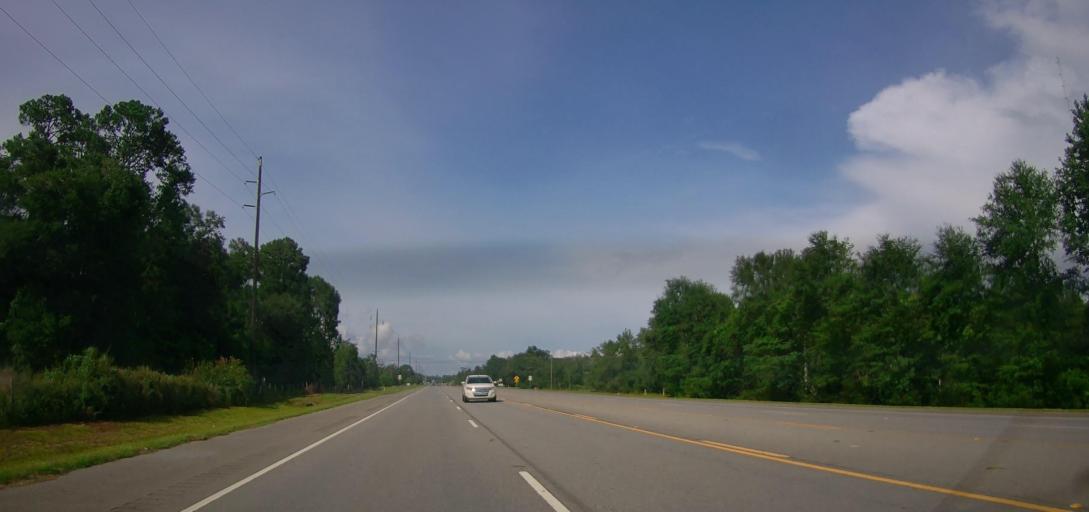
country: US
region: Georgia
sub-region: Wayne County
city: Jesup
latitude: 31.5974
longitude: -81.9372
